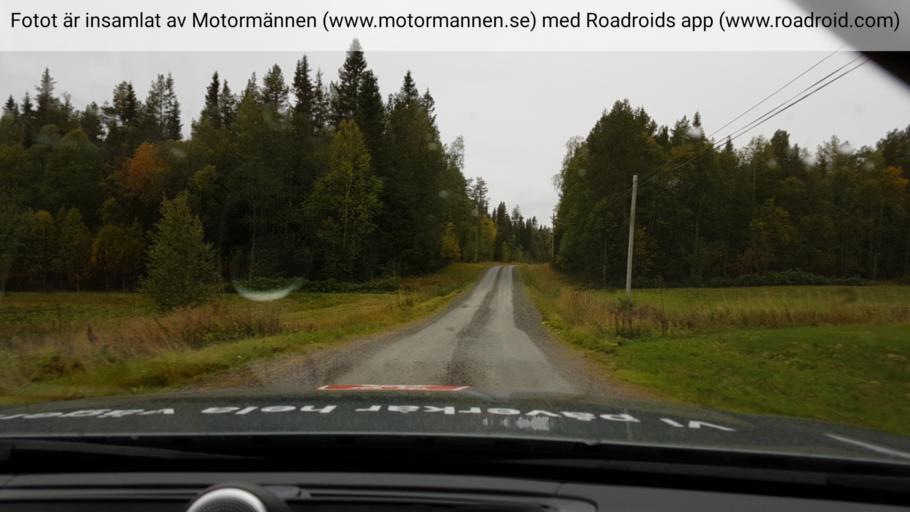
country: NO
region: Nord-Trondelag
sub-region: Lierne
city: Sandvika
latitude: 64.4591
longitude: 14.2559
